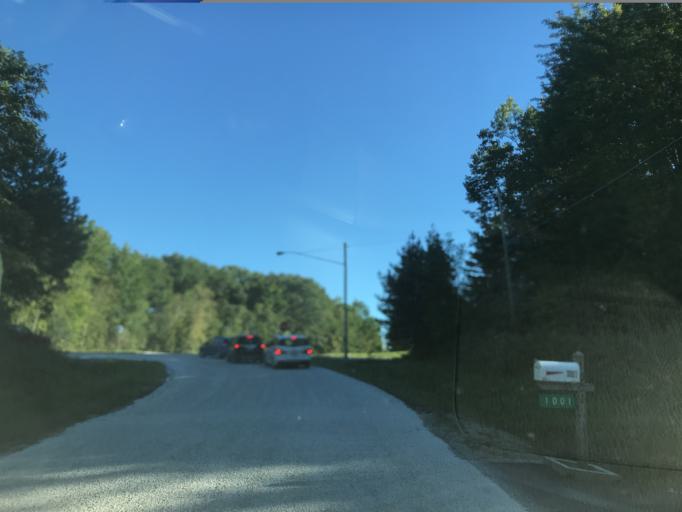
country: US
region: Ohio
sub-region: Ashtabula County
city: Geneva
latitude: 41.7514
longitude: -80.9421
